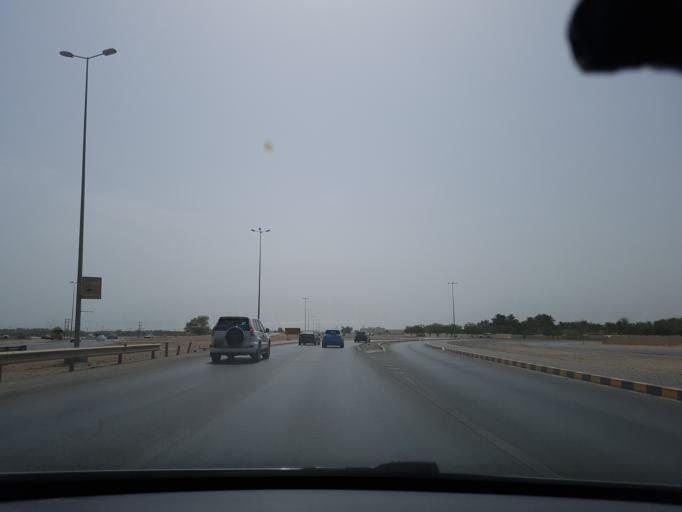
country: OM
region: Al Batinah
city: As Suwayq
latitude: 23.8248
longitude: 57.4220
